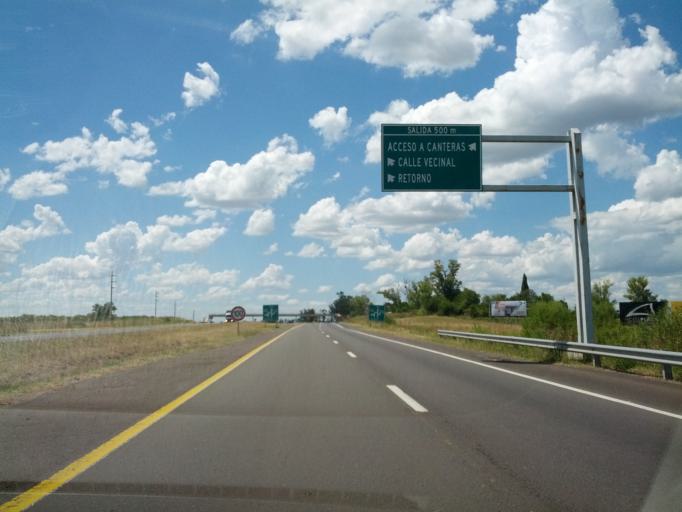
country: AR
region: Entre Rios
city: Concepcion del Uruguay
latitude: -32.4101
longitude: -58.2793
